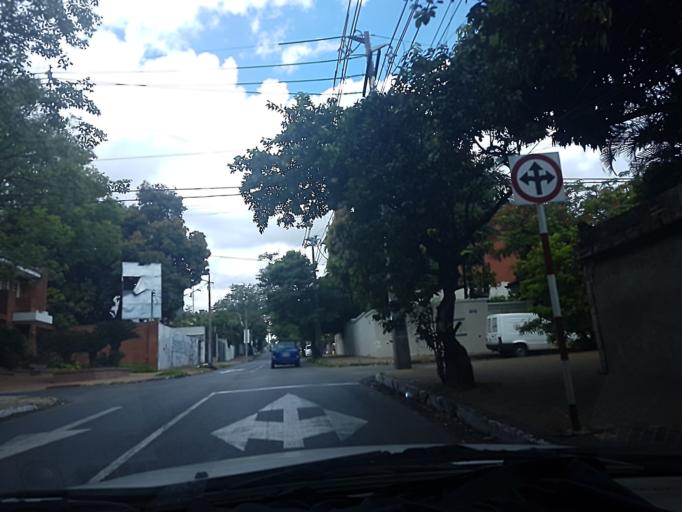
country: PY
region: Asuncion
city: Asuncion
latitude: -25.2848
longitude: -57.6074
